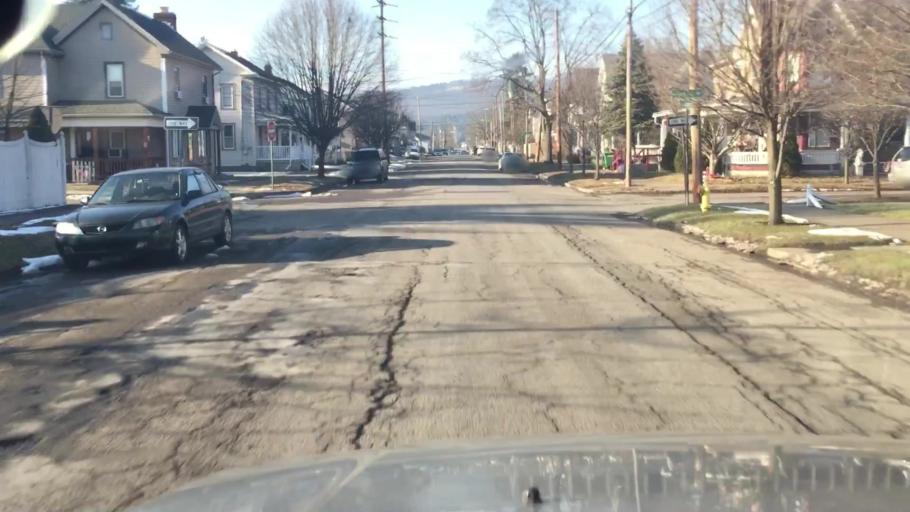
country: US
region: Pennsylvania
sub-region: Columbia County
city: Berwick
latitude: 41.0580
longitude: -76.2314
